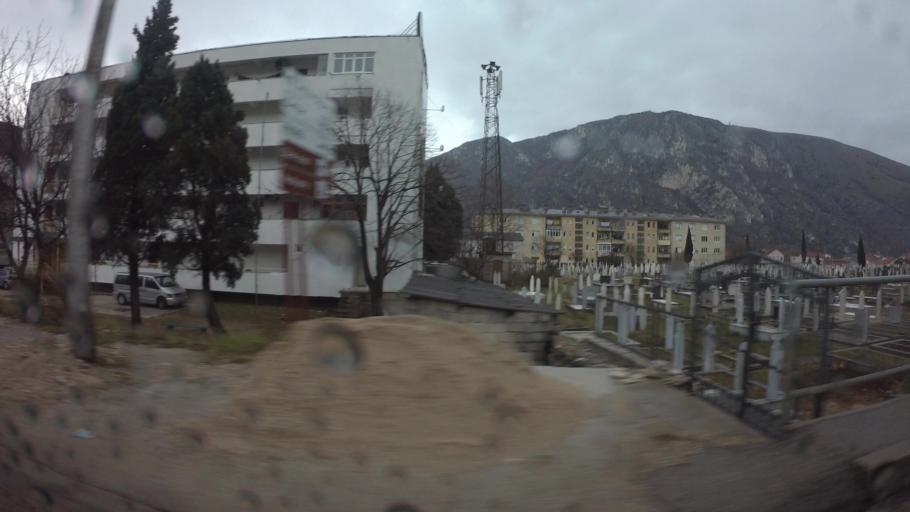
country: BA
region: Federation of Bosnia and Herzegovina
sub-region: Hercegovacko-Bosanski Kanton
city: Mostar
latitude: 43.3288
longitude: 17.8229
